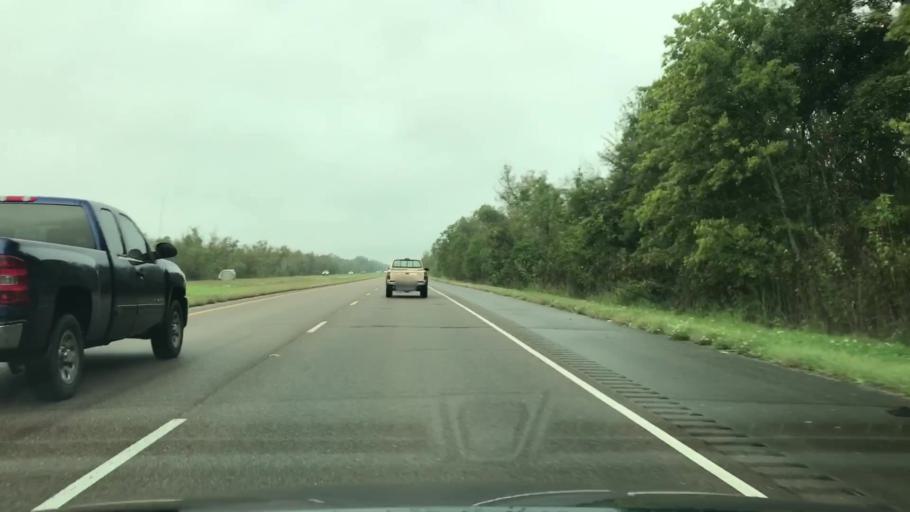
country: US
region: Louisiana
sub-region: Terrebonne Parish
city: Bayou Cane
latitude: 29.6869
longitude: -90.7061
